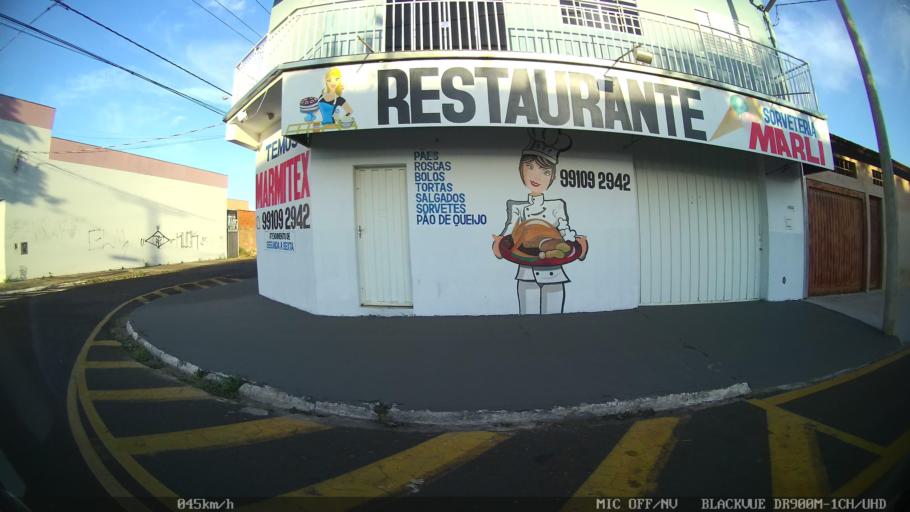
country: BR
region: Sao Paulo
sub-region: Franca
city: Franca
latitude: -20.5127
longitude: -47.3867
